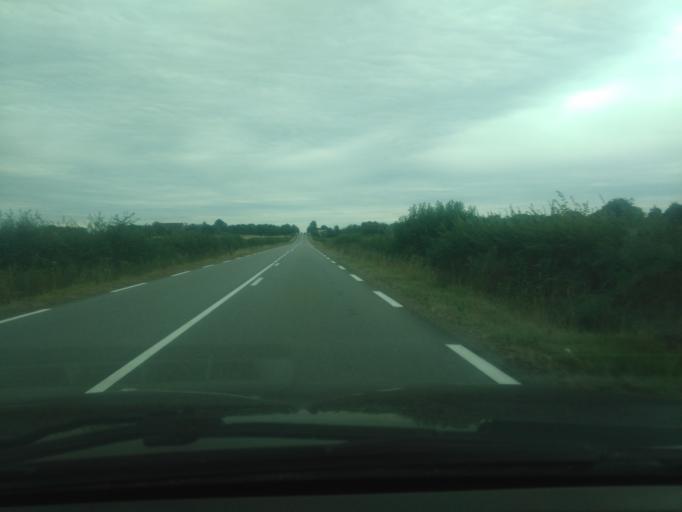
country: FR
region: Centre
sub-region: Departement de l'Indre
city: Neuvy-Saint-Sepulchre
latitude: 46.5834
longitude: 1.8330
